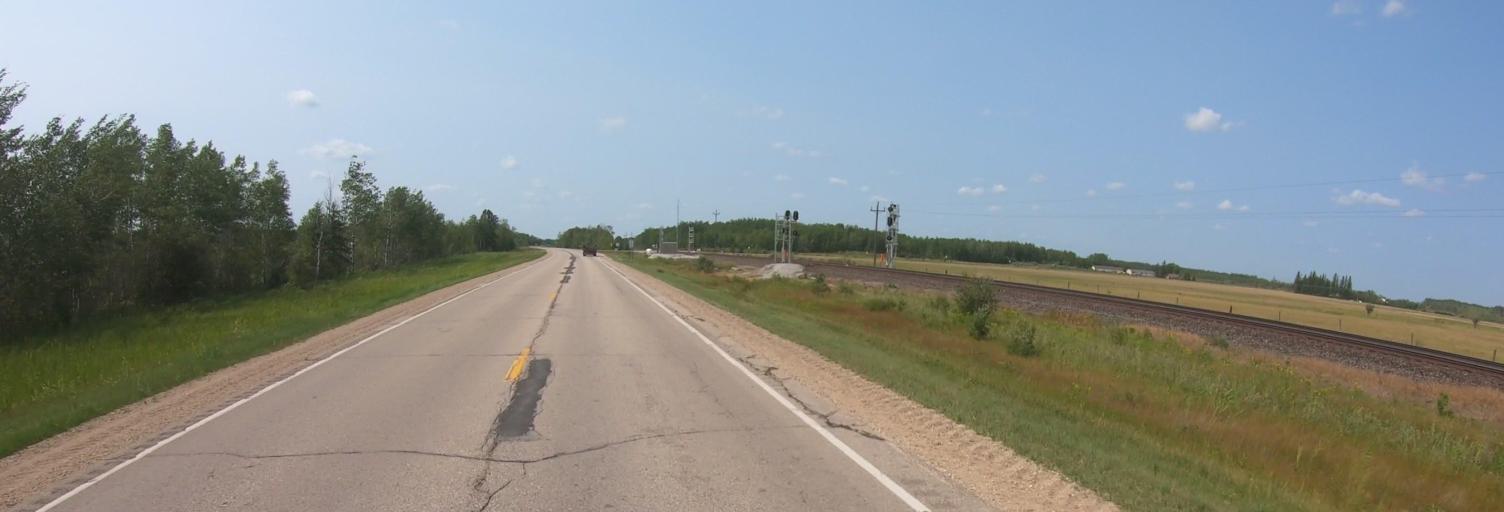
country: US
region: Minnesota
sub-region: Lake of the Woods County
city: Baudette
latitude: 48.7370
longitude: -94.8240
